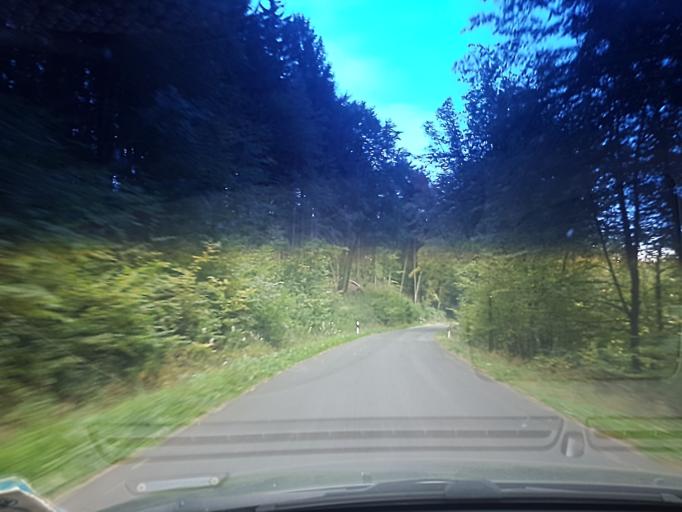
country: DE
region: Bavaria
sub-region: Regierungsbezirk Unterfranken
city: Geiselwind
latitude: 49.8303
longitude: 10.4709
